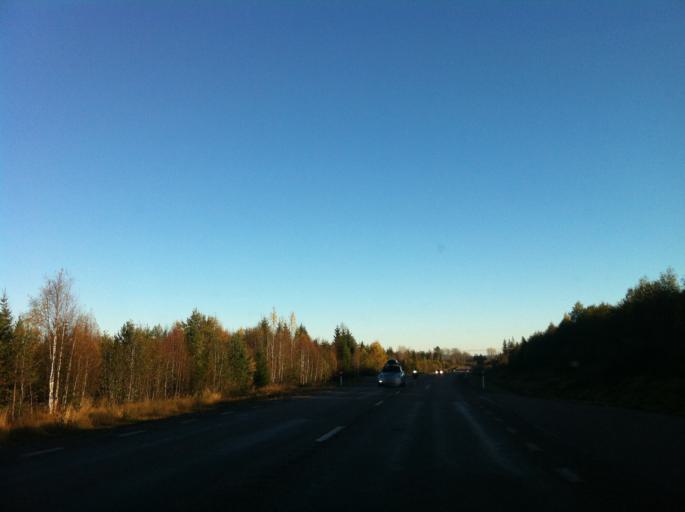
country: SE
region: Dalarna
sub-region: Rattviks Kommun
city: Raettvik
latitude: 60.8384
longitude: 15.2175
